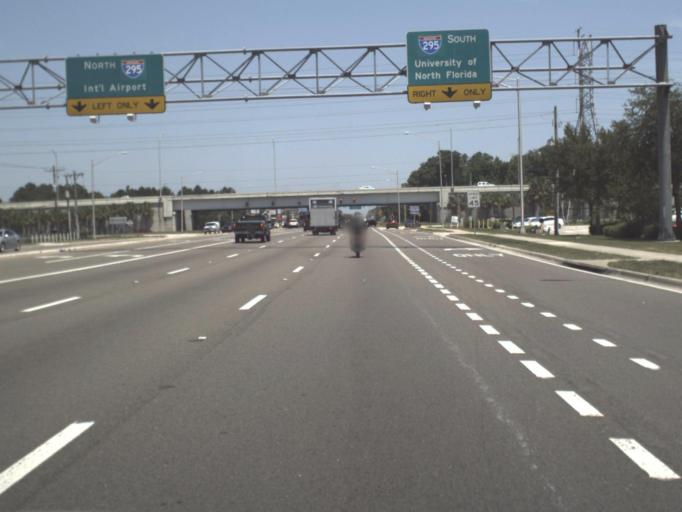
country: US
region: Florida
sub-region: Duval County
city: Neptune Beach
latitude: 30.2868
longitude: -81.5243
